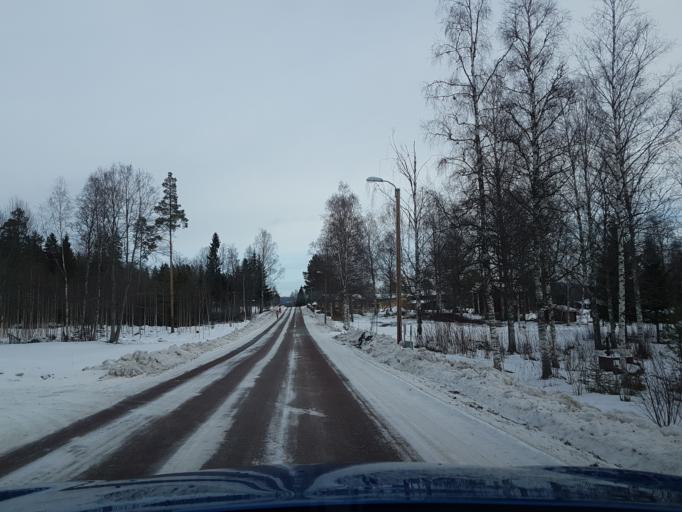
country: SE
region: Dalarna
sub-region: Leksand Municipality
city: Leksand
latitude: 60.7514
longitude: 15.0116
